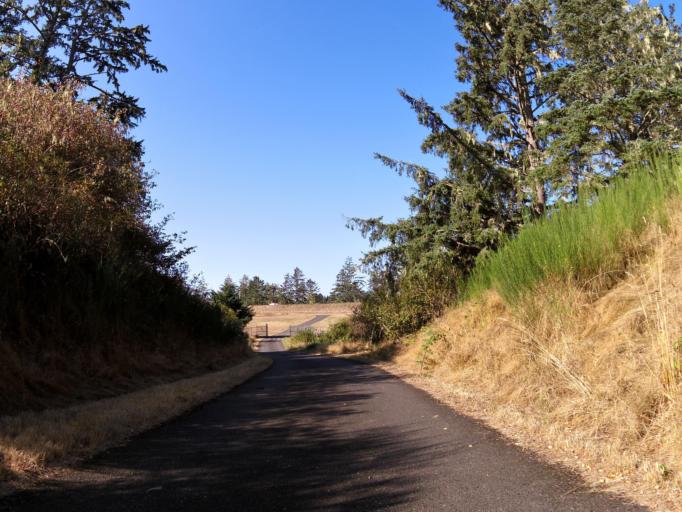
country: US
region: Oregon
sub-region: Clatsop County
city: Warrenton
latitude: 46.1179
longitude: -123.9265
